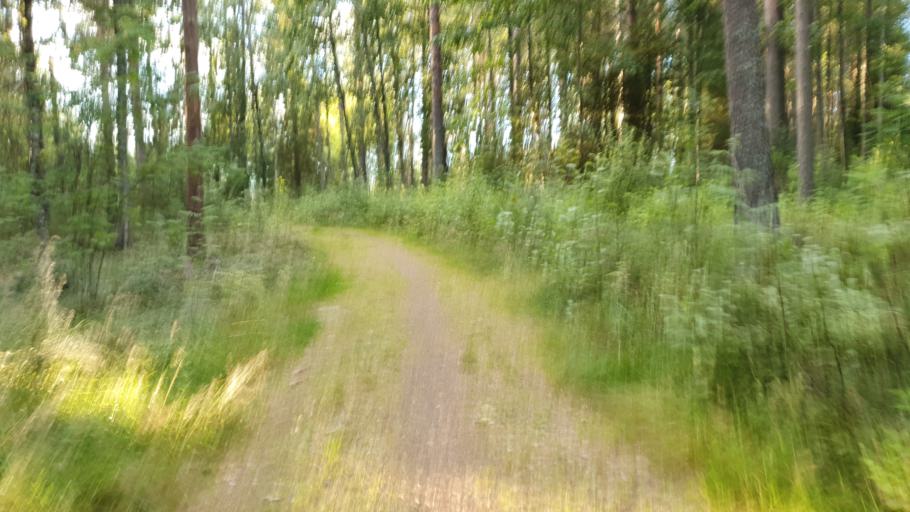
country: FI
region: Kainuu
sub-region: Kehys-Kainuu
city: Kuhmo
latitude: 64.1283
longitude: 29.4935
